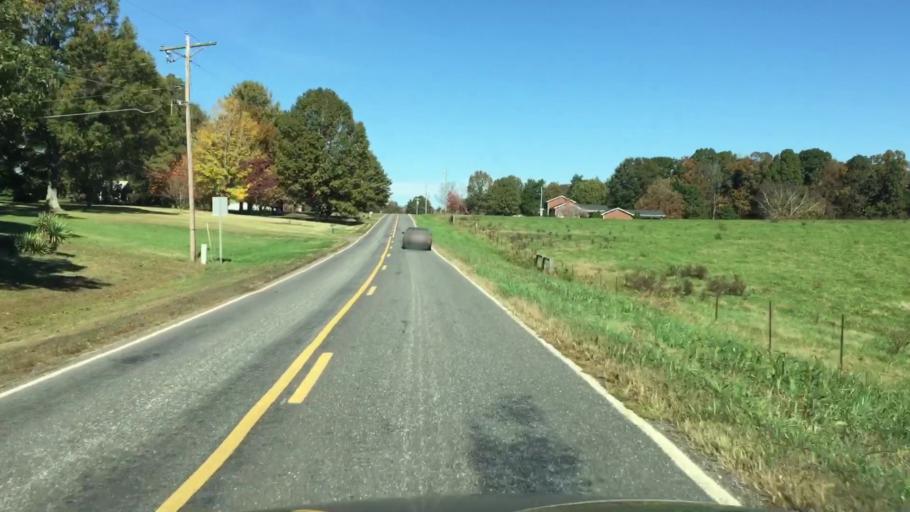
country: US
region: North Carolina
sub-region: Iredell County
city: Mooresville
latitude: 35.5768
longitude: -80.7615
